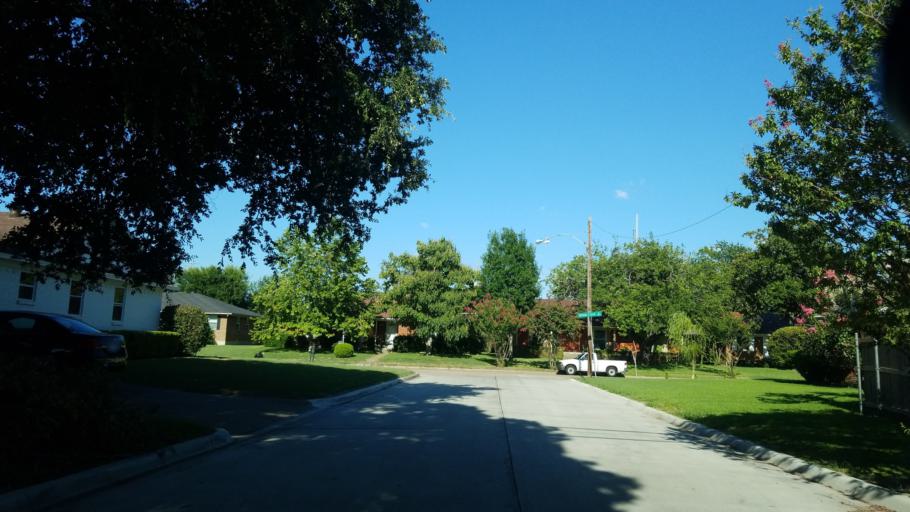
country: US
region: Texas
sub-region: Dallas County
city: Balch Springs
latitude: 32.7863
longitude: -96.7014
